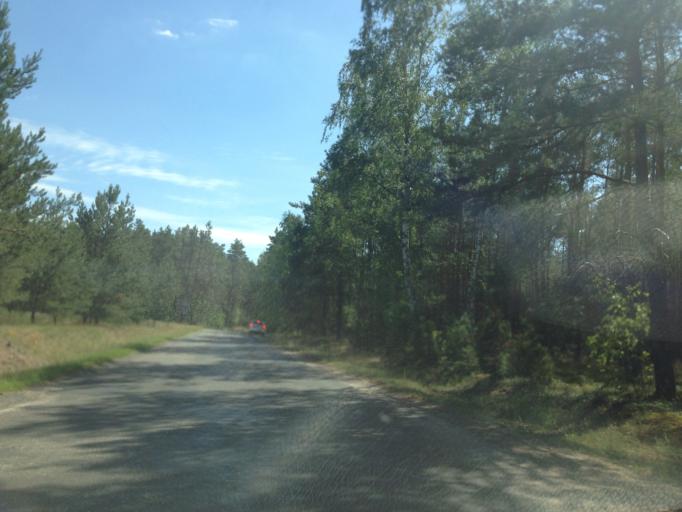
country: PL
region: Kujawsko-Pomorskie
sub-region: Powiat tucholski
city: Sliwice
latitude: 53.6826
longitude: 18.1942
